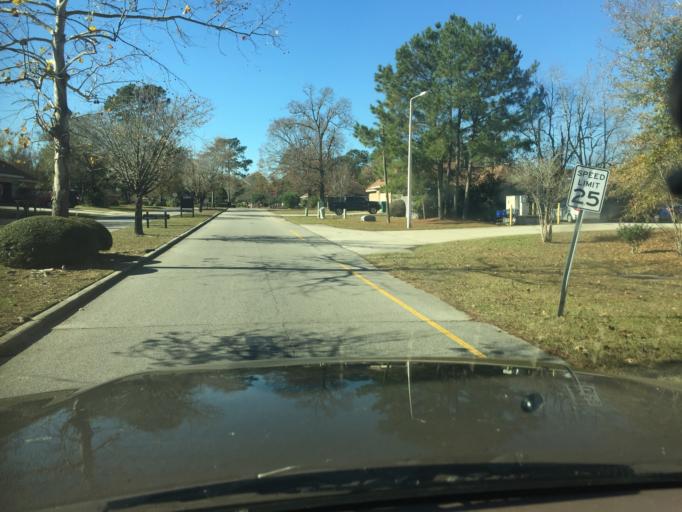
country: US
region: Louisiana
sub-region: Saint Tammany Parish
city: Slidell
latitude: 30.2976
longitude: -89.7223
